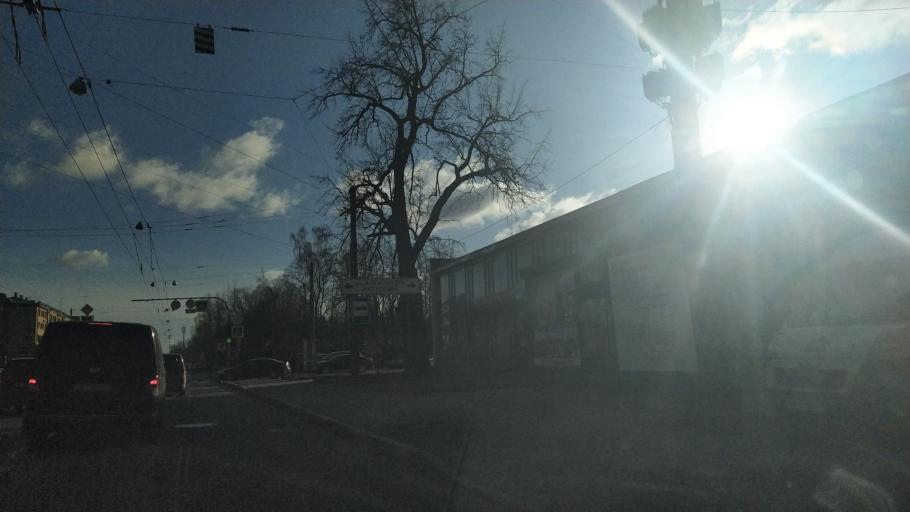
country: RU
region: Leningrad
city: Sampsonievskiy
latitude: 59.9825
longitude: 30.3430
